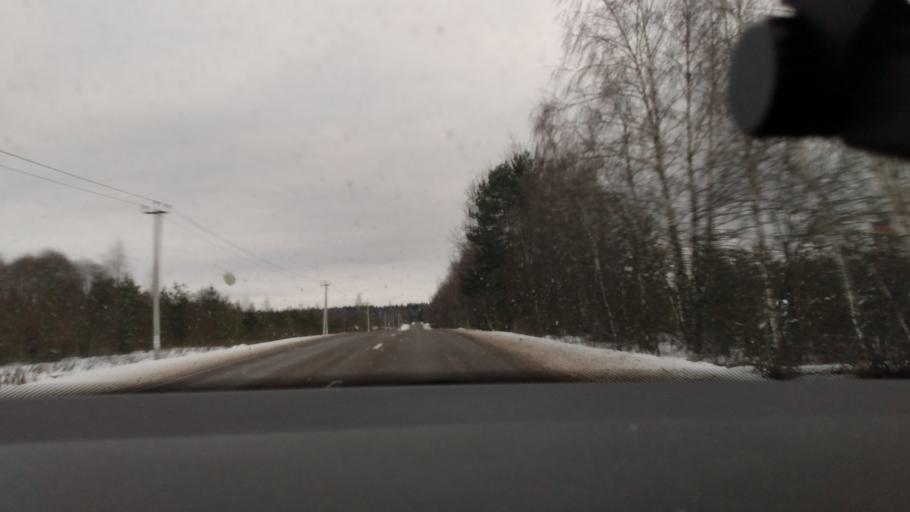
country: RU
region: Moskovskaya
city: Yegor'yevsk
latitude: 55.2327
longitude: 39.0677
